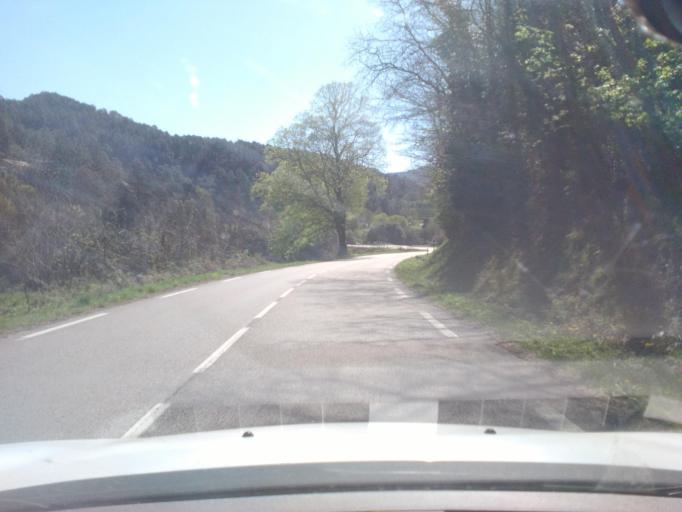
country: FR
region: Languedoc-Roussillon
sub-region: Departement du Gard
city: Lasalle
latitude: 44.1126
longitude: 3.7789
